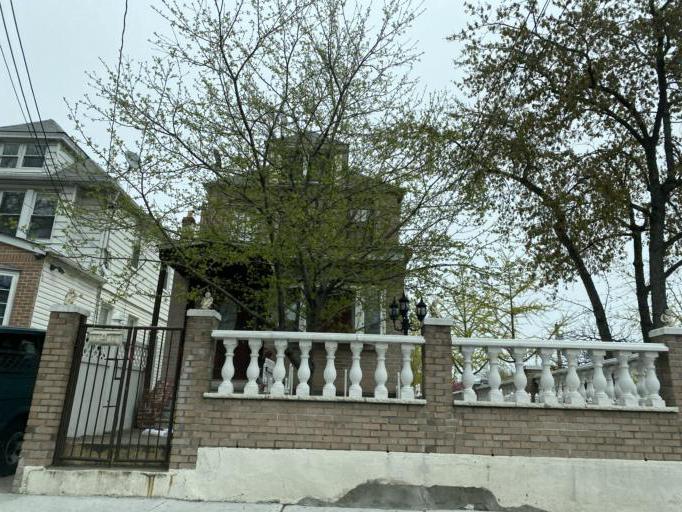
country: US
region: New York
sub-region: Queens County
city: Borough of Queens
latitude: 40.6753
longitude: -73.8252
